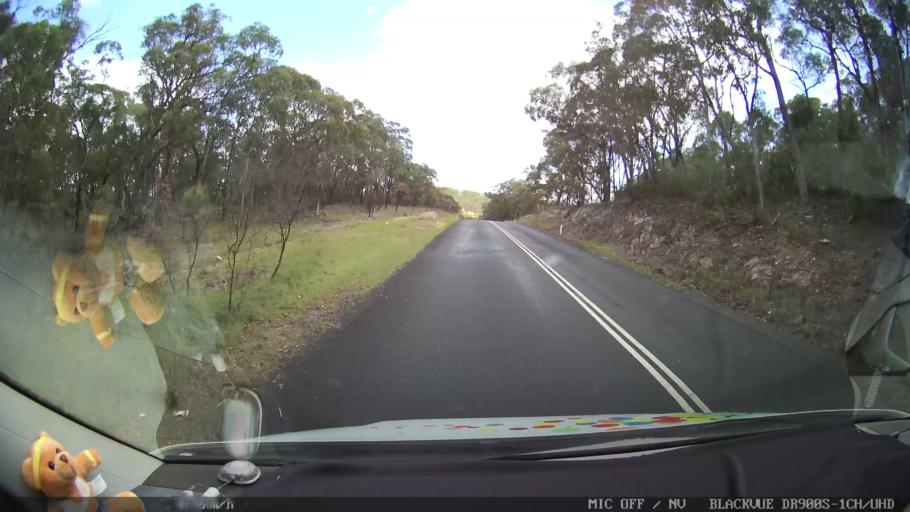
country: AU
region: New South Wales
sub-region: Glen Innes Severn
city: Glen Innes
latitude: -29.5427
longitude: 151.6690
